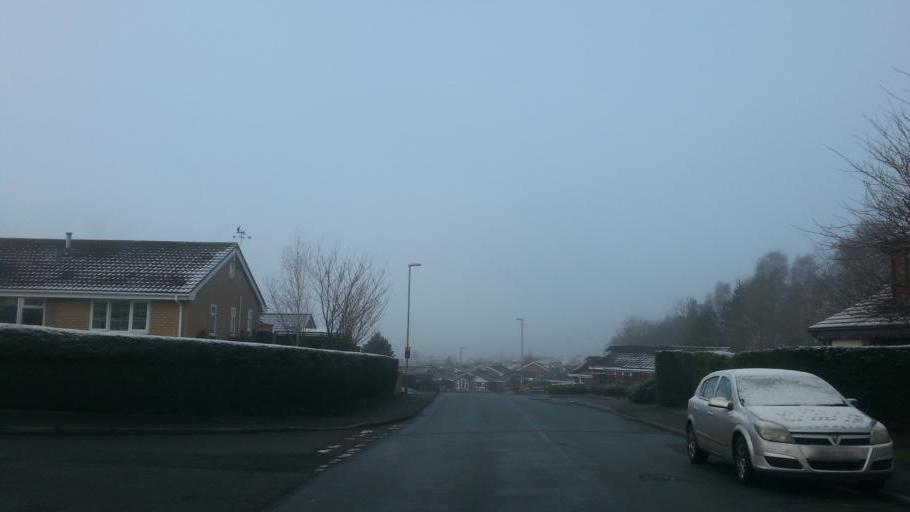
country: GB
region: England
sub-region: Staffordshire
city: Biddulph
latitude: 53.1210
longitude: -2.1609
